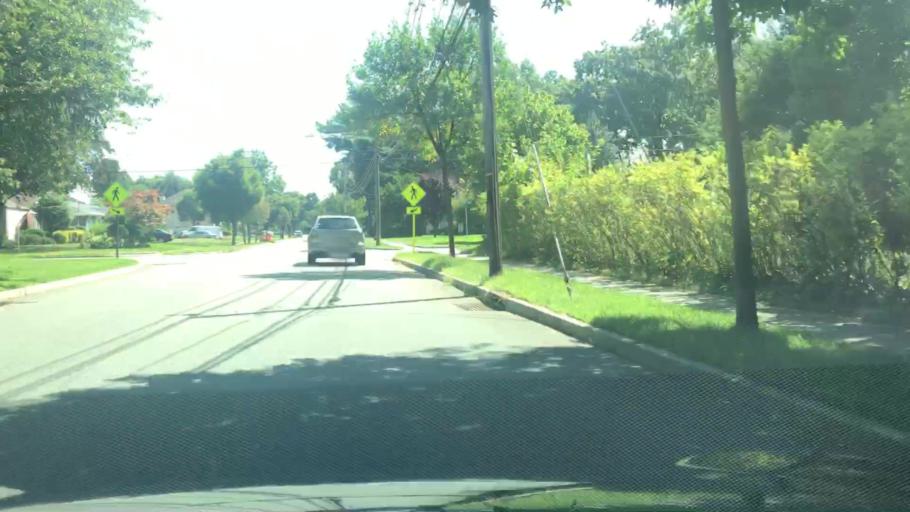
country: US
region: New Jersey
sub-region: Bergen County
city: River Edge
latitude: 40.9221
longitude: -74.0483
